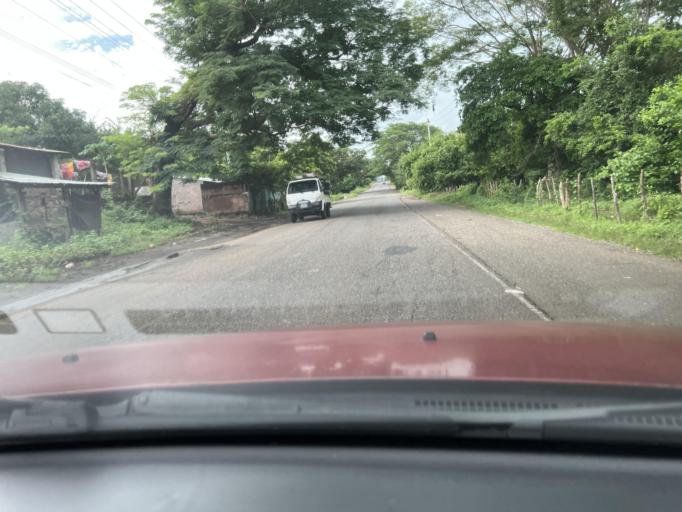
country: SV
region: La Union
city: San Alejo
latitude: 13.4111
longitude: -87.8905
